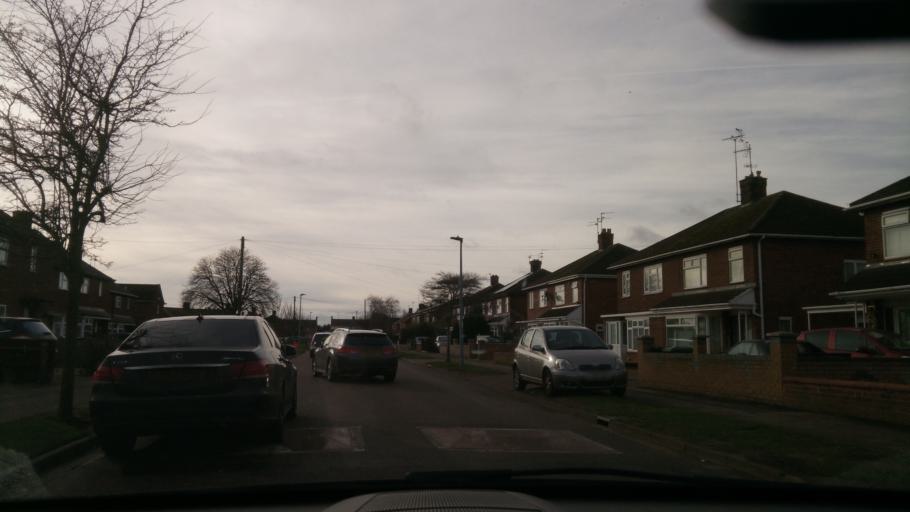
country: GB
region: England
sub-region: Peterborough
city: Peterborough
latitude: 52.5861
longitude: -0.2213
